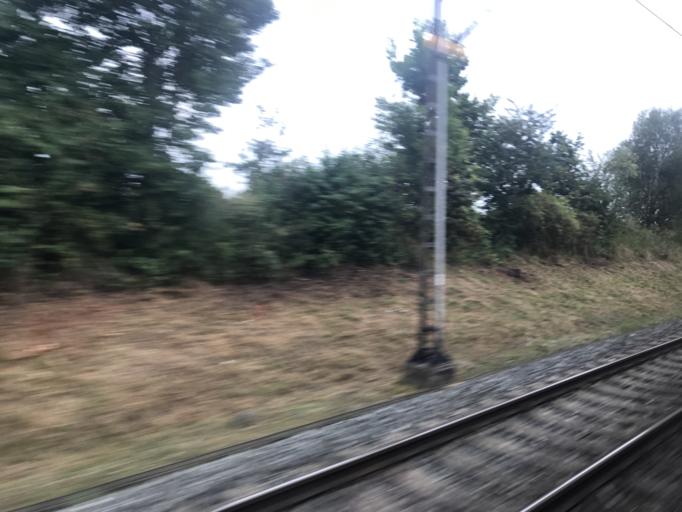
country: DE
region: Bavaria
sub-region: Regierungsbezirk Unterfranken
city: Bergtheim
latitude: 49.9047
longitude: 10.0782
